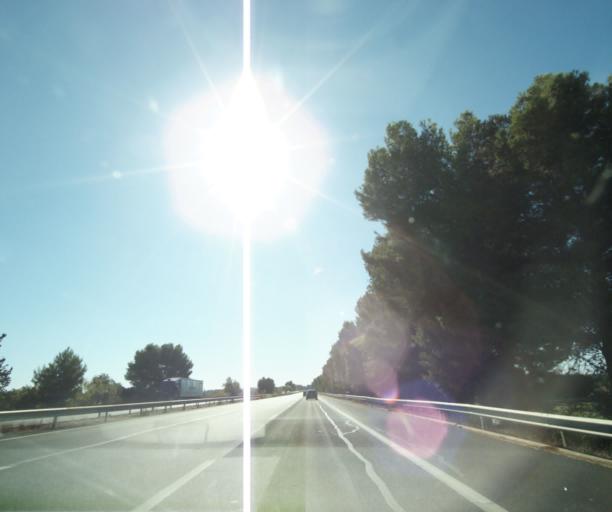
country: FR
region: Languedoc-Roussillon
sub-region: Departement de l'Herault
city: Villeneuve-les-Beziers
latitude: 43.3214
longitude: 3.2668
